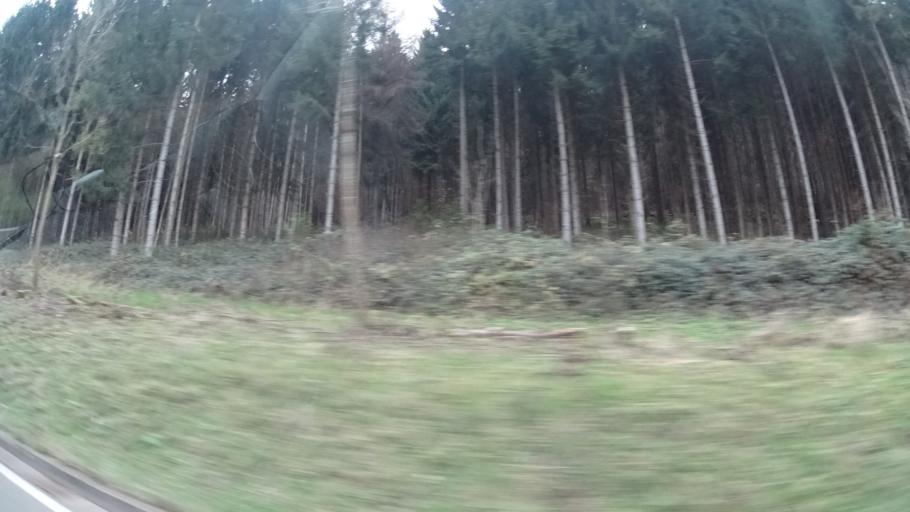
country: DE
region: Baden-Wuerttemberg
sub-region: Karlsruhe Region
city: Eberbach
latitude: 49.4416
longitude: 8.9548
